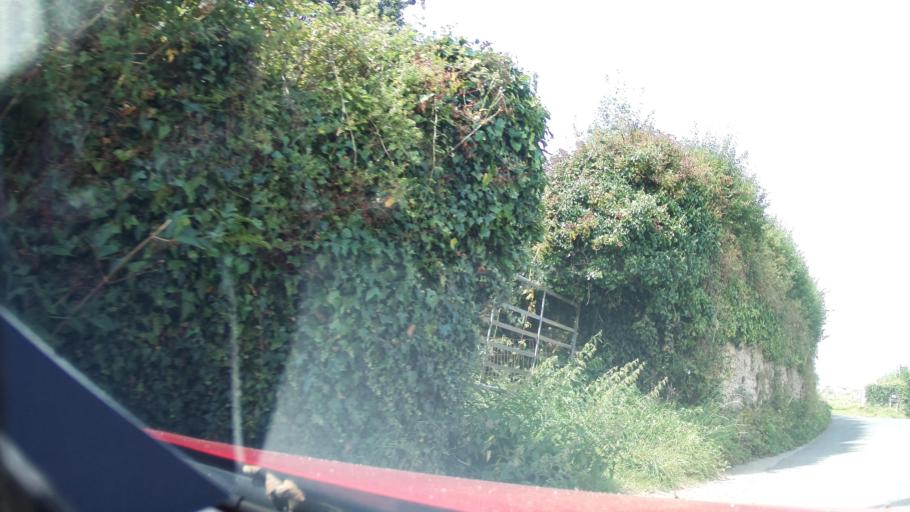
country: GB
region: England
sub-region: Devon
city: Marldon
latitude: 50.4078
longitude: -3.6105
